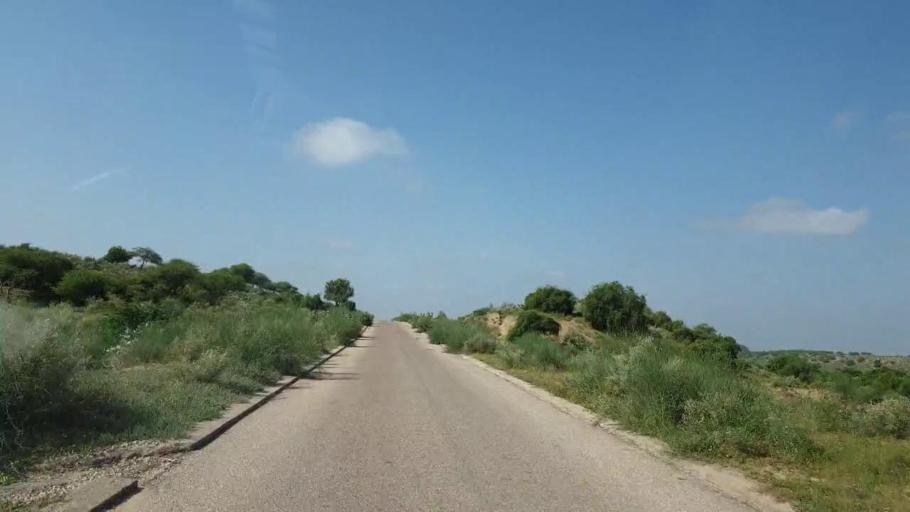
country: PK
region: Sindh
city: Mithi
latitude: 24.5567
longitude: 69.8951
